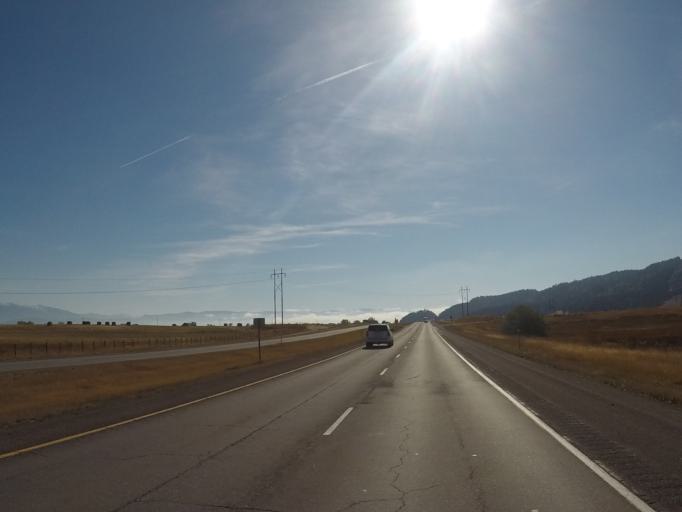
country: US
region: Montana
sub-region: Flathead County
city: Somers
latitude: 48.1139
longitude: -114.2528
